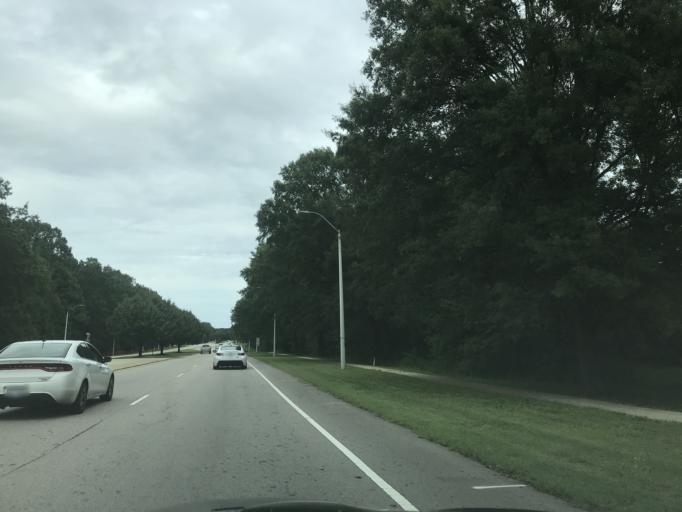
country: US
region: North Carolina
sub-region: Wake County
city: Cary
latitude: 35.7764
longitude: -78.7595
